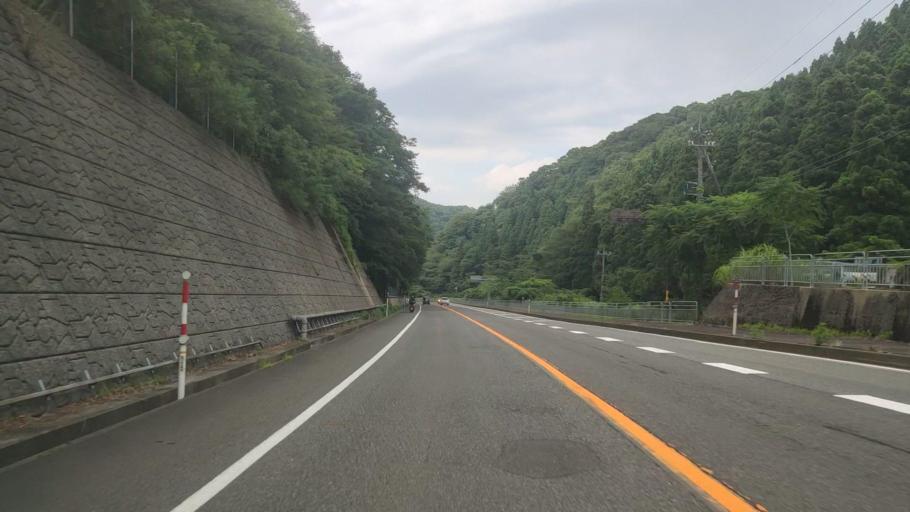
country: JP
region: Fukui
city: Takefu
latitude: 35.8051
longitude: 136.0946
